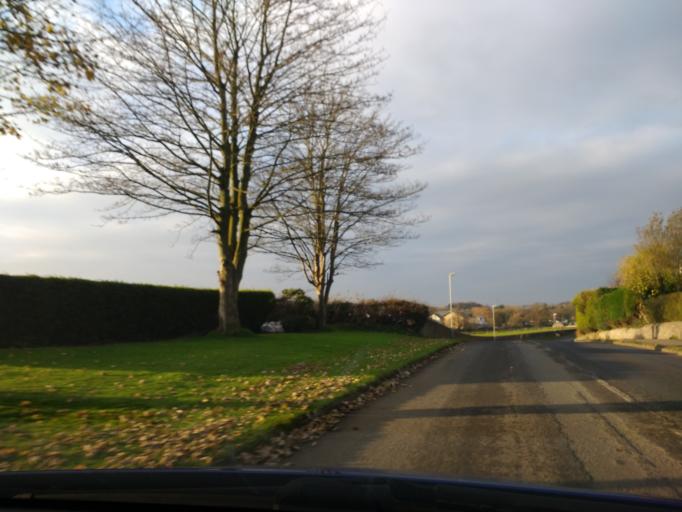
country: GB
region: England
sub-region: Lancashire
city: Bolton le Sands
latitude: 54.0782
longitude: -2.7532
